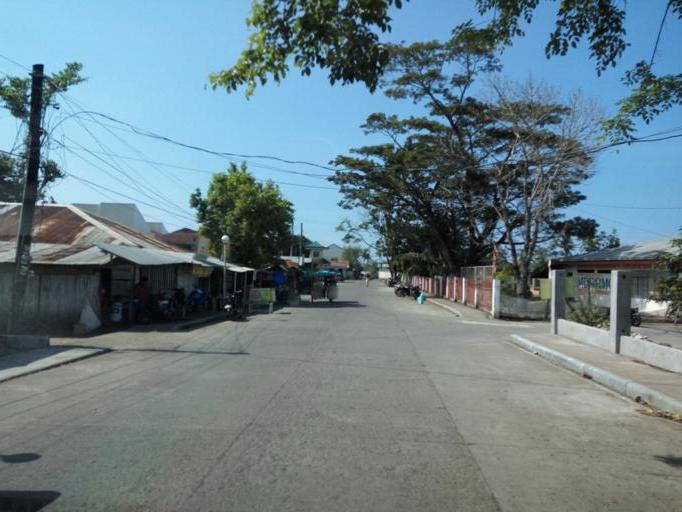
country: PH
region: Cagayan Valley
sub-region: Province of Cagayan
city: Gonzaga
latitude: 18.2604
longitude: 121.9966
